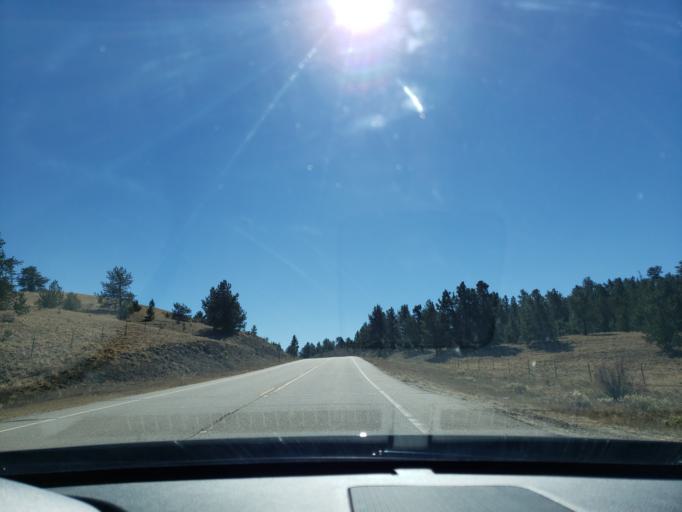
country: US
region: Colorado
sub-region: Chaffee County
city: Buena Vista
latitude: 38.8699
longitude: -105.6680
